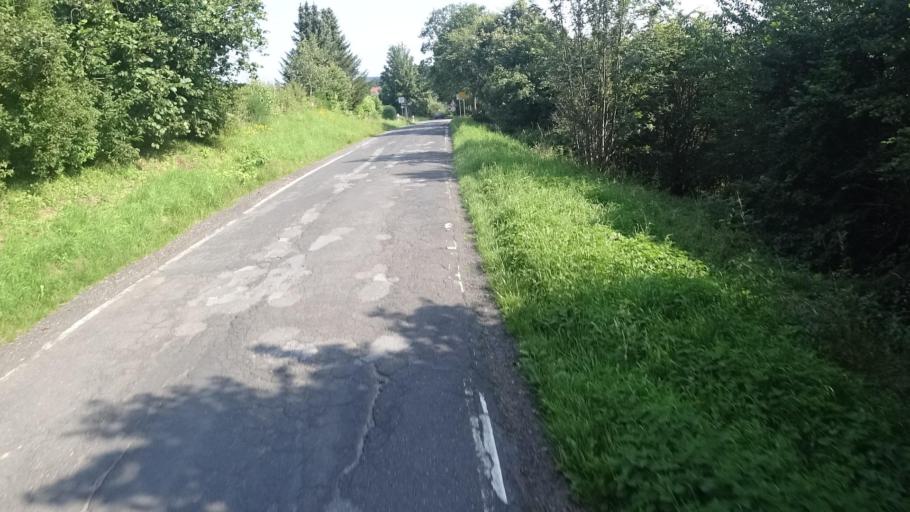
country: DE
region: Rheinland-Pfalz
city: Sankt Katharinen
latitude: 50.5607
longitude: 7.3549
